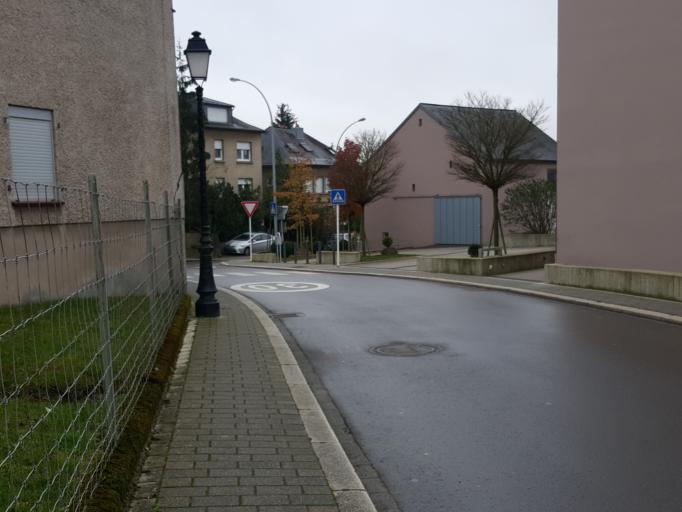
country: LU
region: Luxembourg
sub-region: Canton de Luxembourg
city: Alzingen
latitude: 49.5693
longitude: 6.1641
